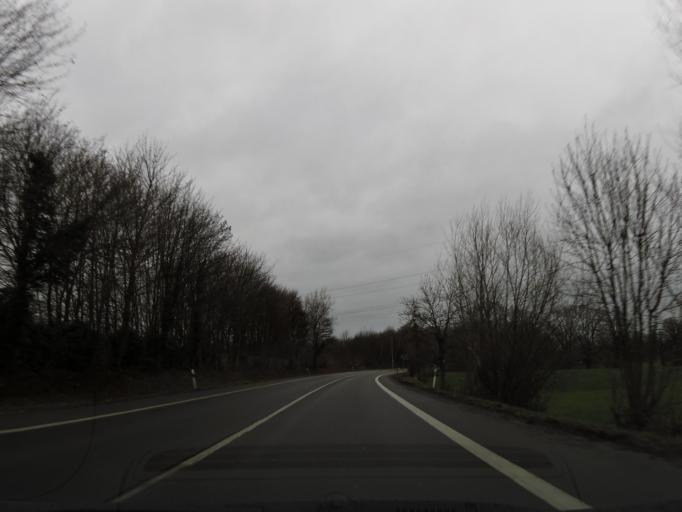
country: DE
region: North Rhine-Westphalia
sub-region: Regierungsbezirk Koln
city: Aachen
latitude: 50.8147
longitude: 6.0698
